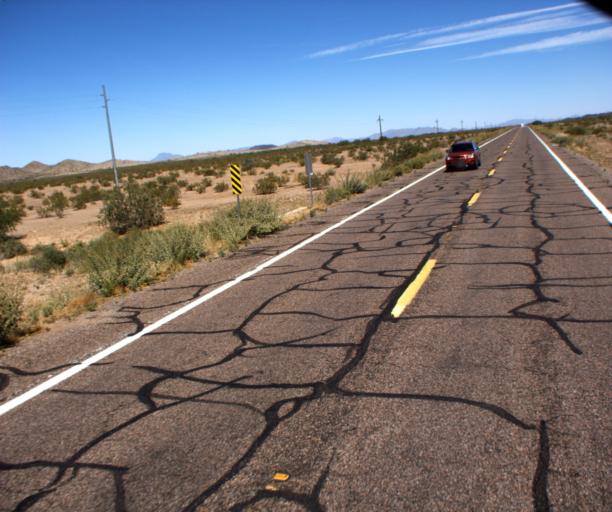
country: US
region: Arizona
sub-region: Maricopa County
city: Gila Bend
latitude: 32.7625
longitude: -112.8205
